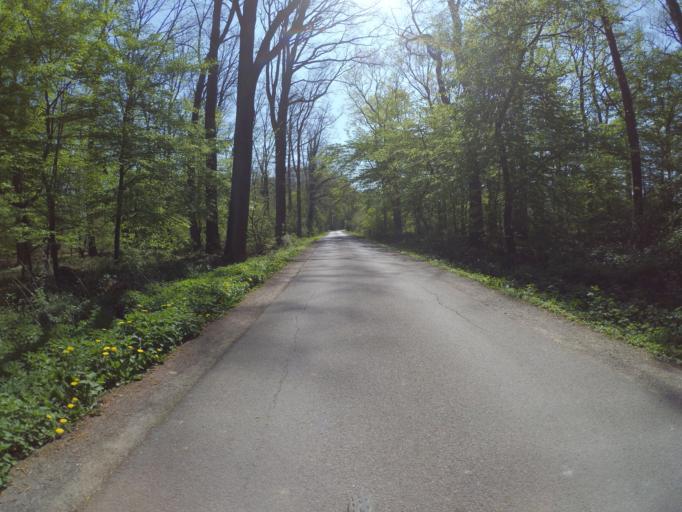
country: DE
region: North Rhine-Westphalia
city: Ludinghausen
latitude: 51.7600
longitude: 7.4388
